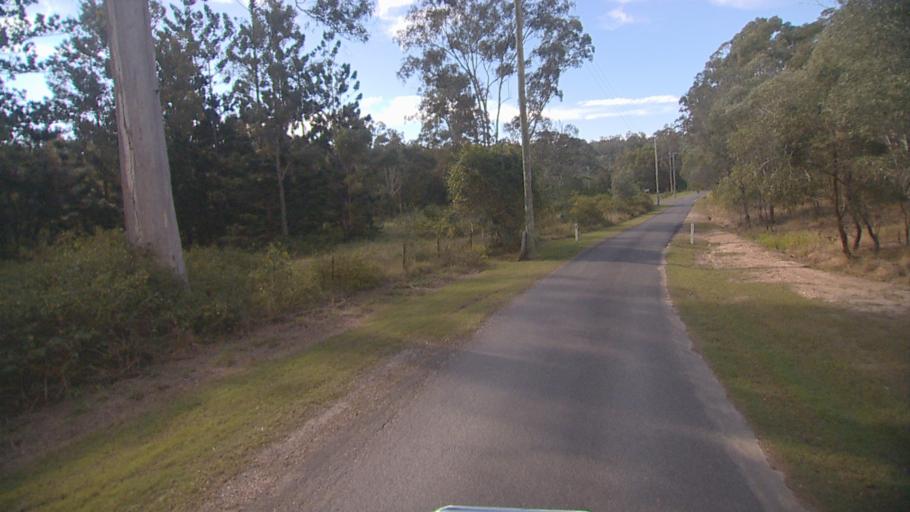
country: AU
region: Queensland
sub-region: Logan
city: Windaroo
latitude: -27.7763
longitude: 153.1749
